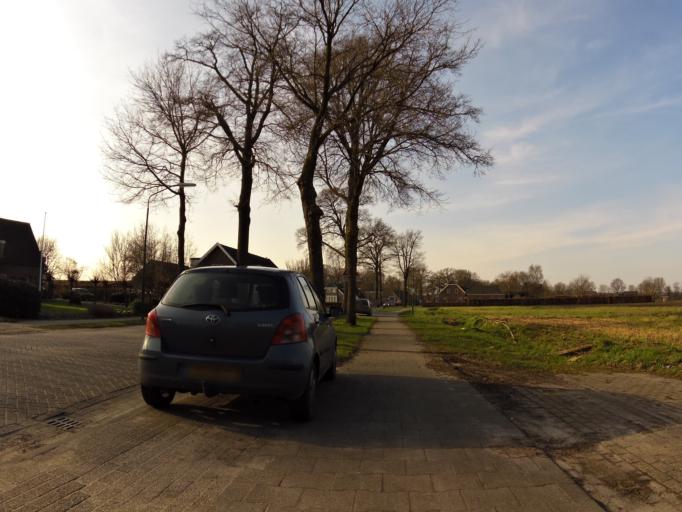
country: NL
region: North Brabant
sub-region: Gemeente Haaren
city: Haaren
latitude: 51.6394
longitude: 5.2295
